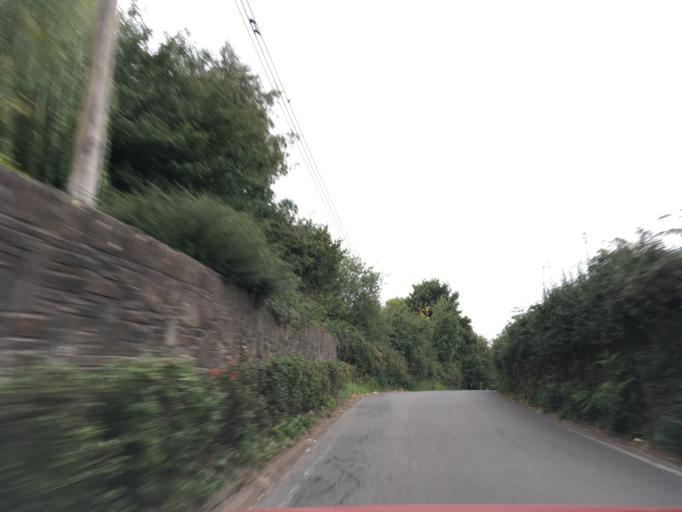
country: GB
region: Wales
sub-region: Newport
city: Marshfield
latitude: 51.5471
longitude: -3.0904
